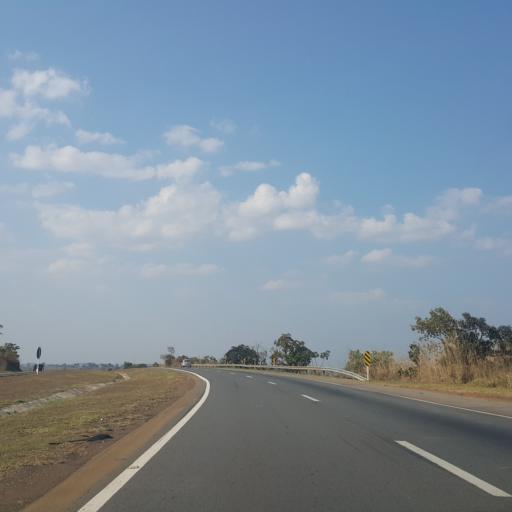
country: BR
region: Goias
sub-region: Abadiania
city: Abadiania
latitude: -16.1828
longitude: -48.6546
